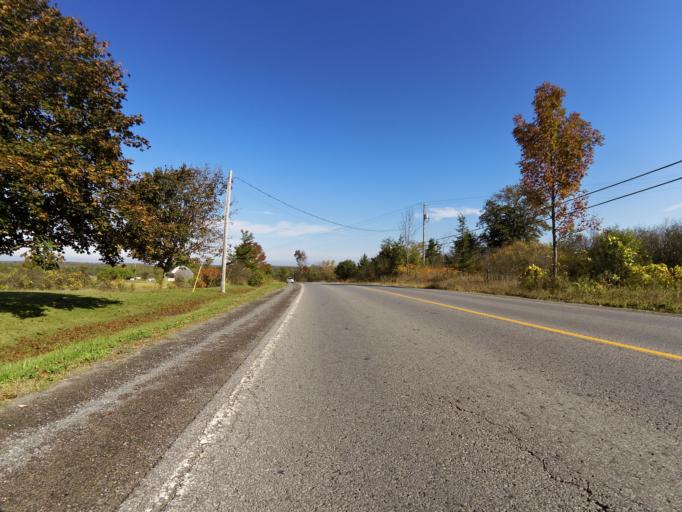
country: CA
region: Ontario
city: Prince Edward
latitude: 44.0108
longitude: -77.3634
